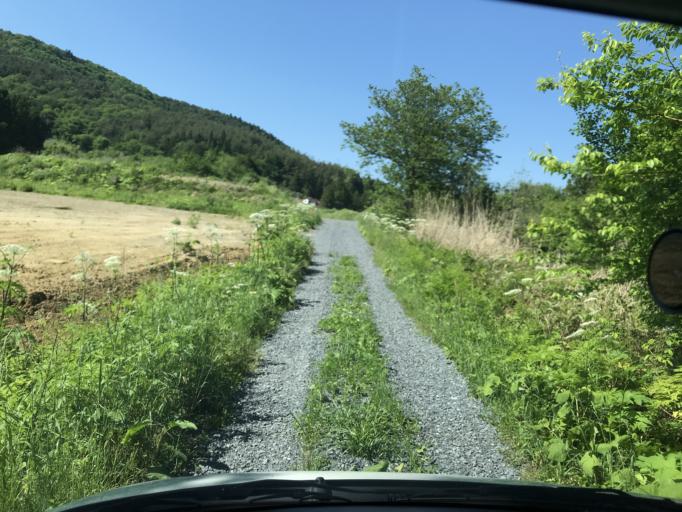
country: JP
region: Iwate
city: Ichinoseki
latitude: 38.9862
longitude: 141.2149
